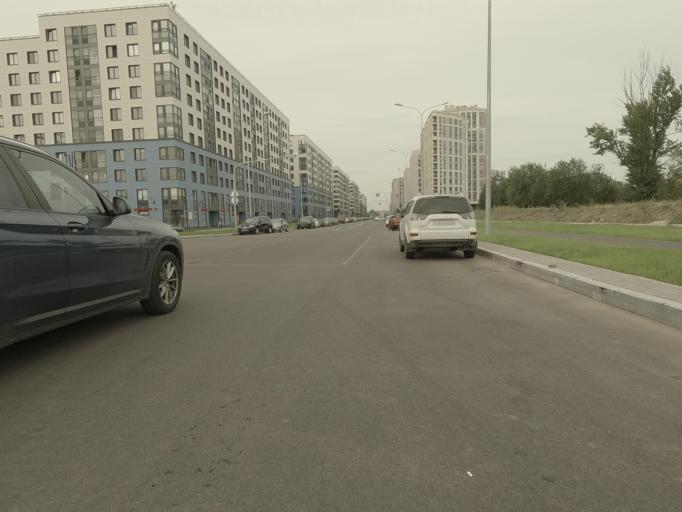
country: RU
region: St.-Petersburg
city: Admiralteisky
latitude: 59.8972
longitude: 30.3122
